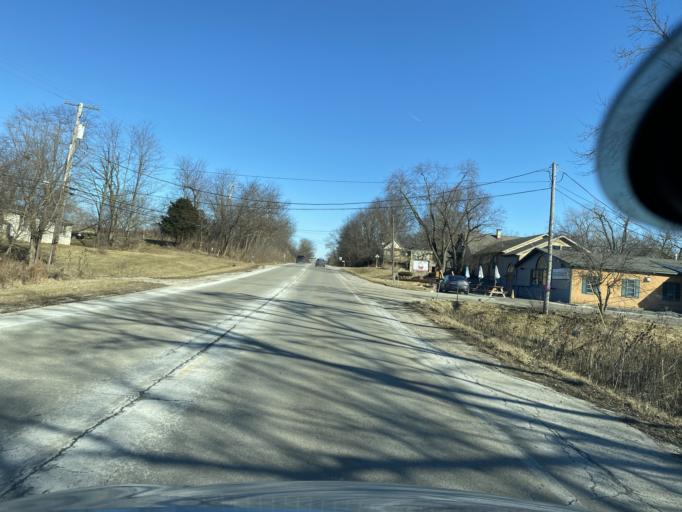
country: US
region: Illinois
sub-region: Will County
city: Lockport
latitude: 41.6147
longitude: -88.0374
